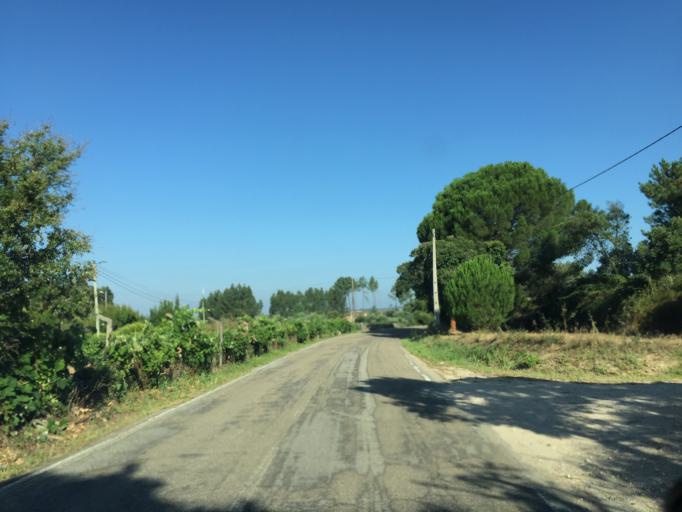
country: PT
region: Santarem
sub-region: Abrantes
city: Alferrarede
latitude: 39.5337
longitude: -8.1392
